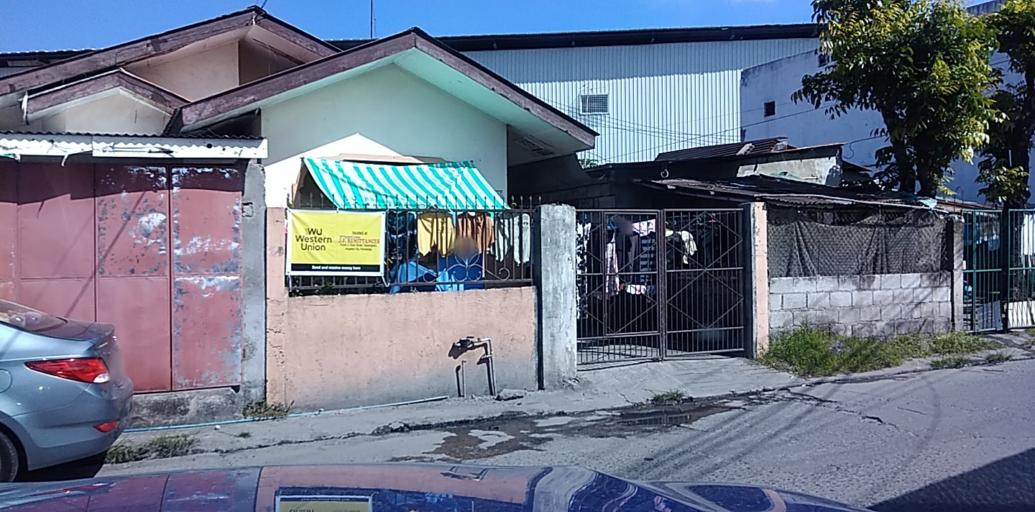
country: PH
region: Central Luzon
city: Santol
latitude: 15.1722
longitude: 120.5171
